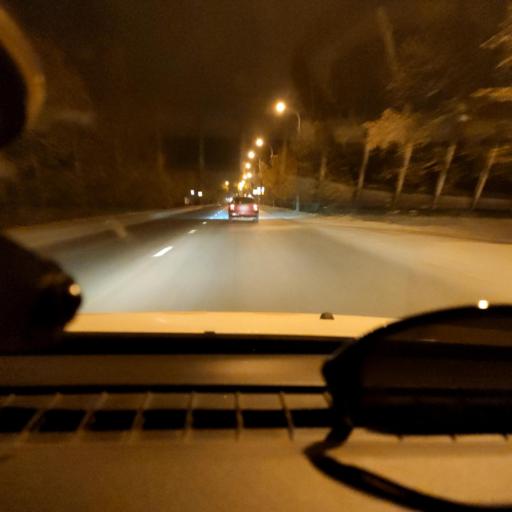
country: RU
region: Samara
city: Rozhdestveno
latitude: 53.1540
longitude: 50.0695
